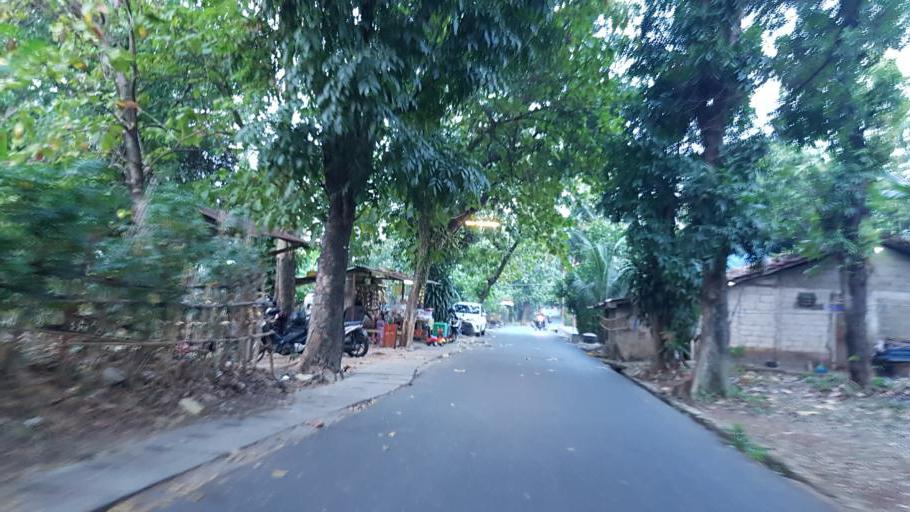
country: ID
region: West Java
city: Pamulang
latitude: -6.3130
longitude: 106.7825
